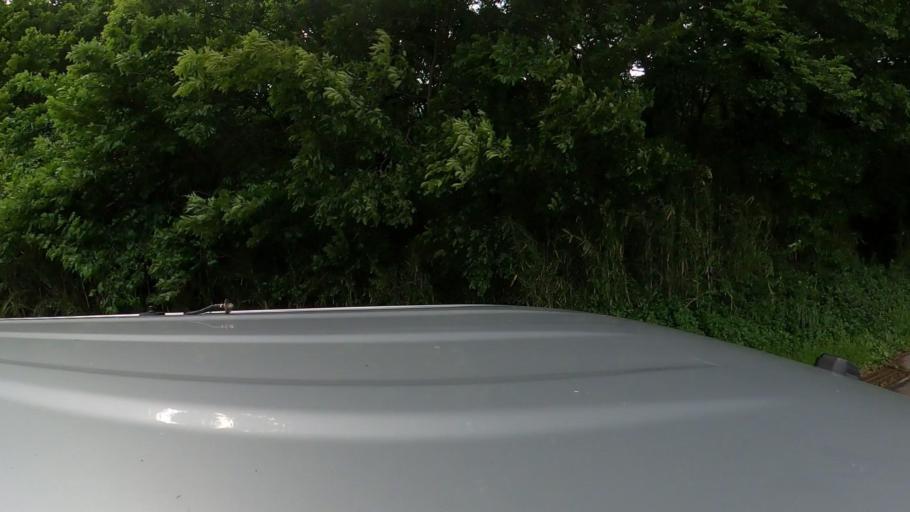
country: JP
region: Ibaraki
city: Ami
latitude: 35.9820
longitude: 140.2433
